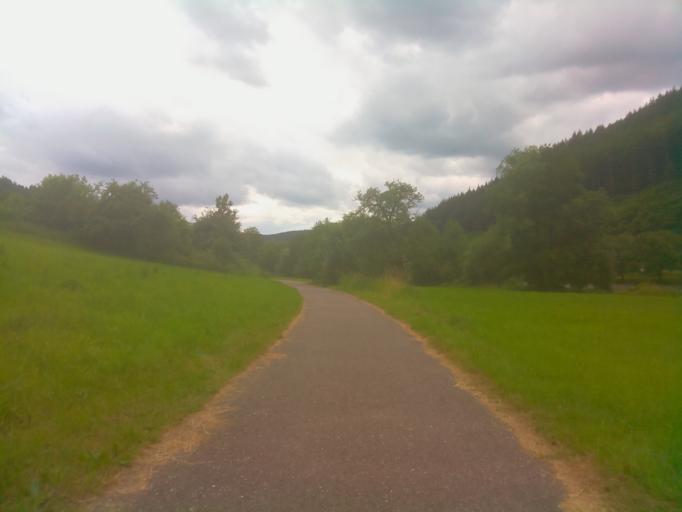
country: DE
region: Hesse
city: Neckarsteinach
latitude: 49.4115
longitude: 8.8733
